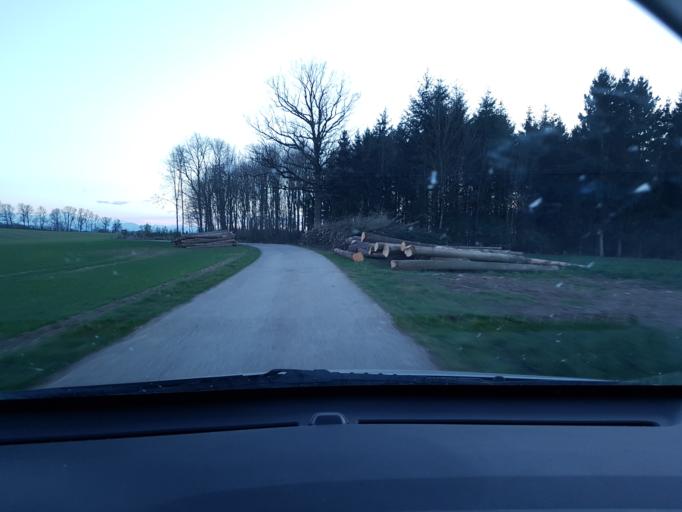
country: AT
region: Upper Austria
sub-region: Politischer Bezirk Linz-Land
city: Ansfelden
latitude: 48.1779
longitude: 14.3211
